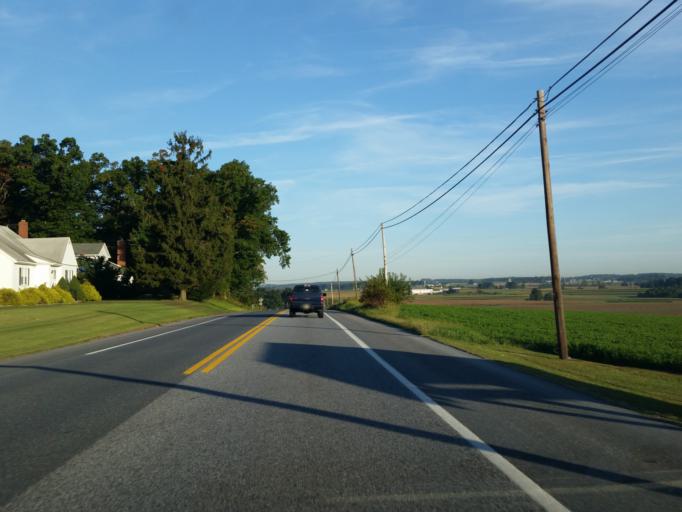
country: US
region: Pennsylvania
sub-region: Lancaster County
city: Quarryville
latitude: 39.8218
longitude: -76.2006
